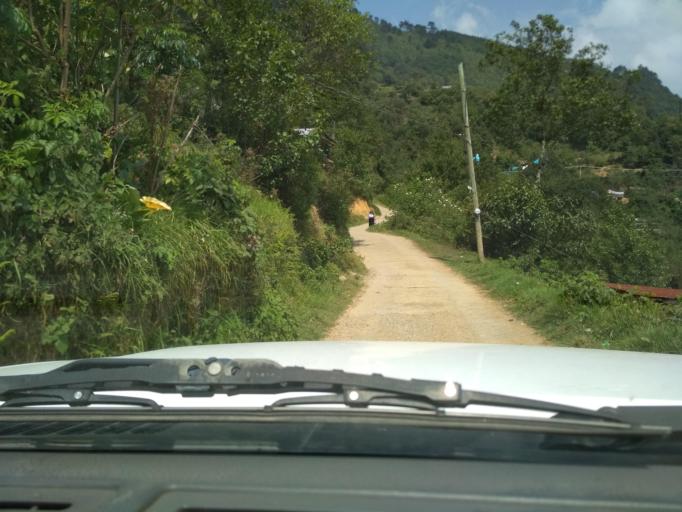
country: MX
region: Veracruz
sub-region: Camerino Z. Mendoza
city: Necoxtla
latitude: 18.7688
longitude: -97.1505
